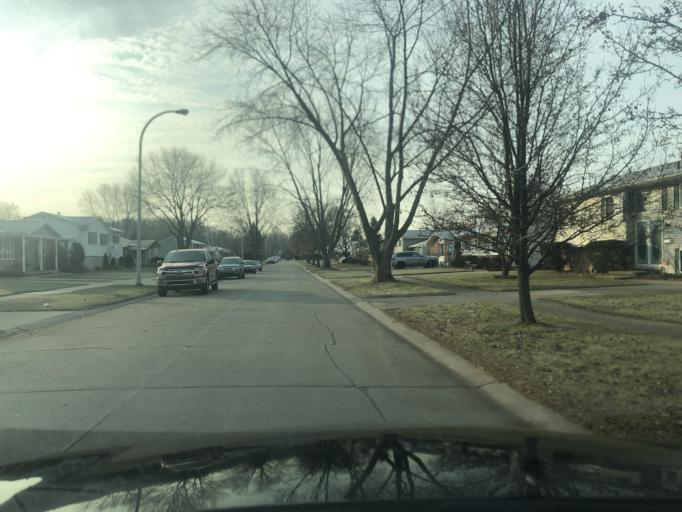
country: US
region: Michigan
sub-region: Wayne County
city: Romulus
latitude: 42.1914
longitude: -83.3351
